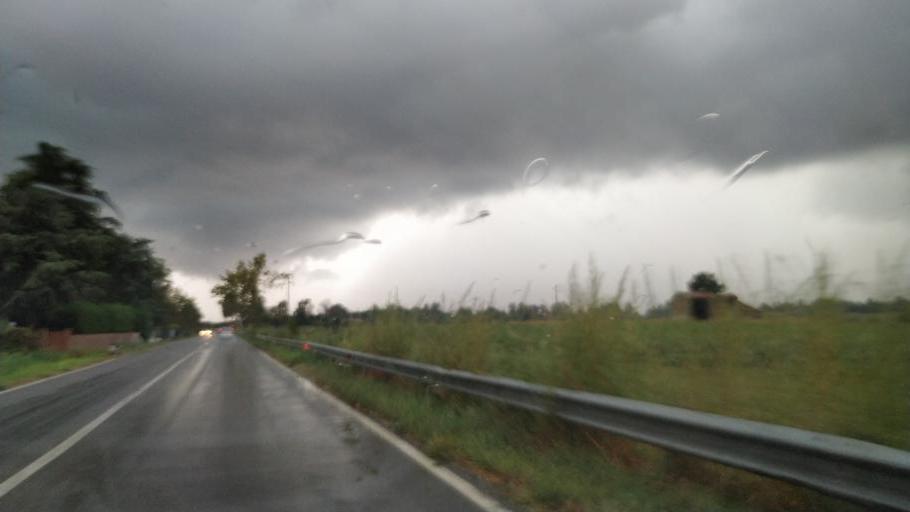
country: IT
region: Emilia-Romagna
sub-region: Provincia di Ferrara
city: Pontegradella
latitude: 44.8522
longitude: 11.6702
